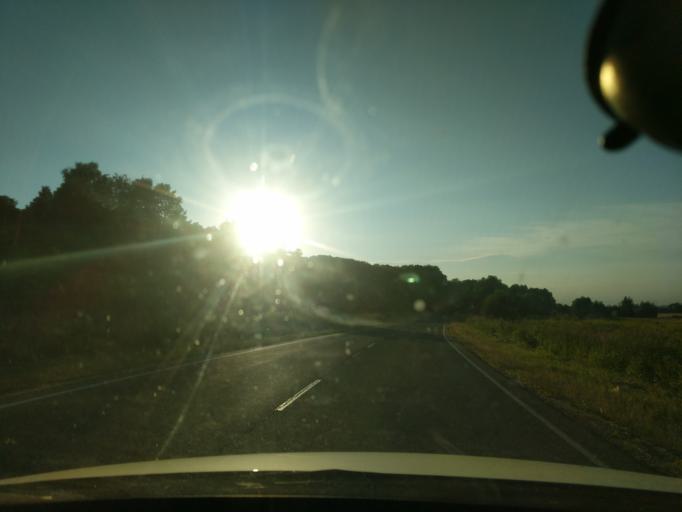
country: RU
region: Moskovskaya
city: Danki
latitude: 54.8508
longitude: 37.4916
